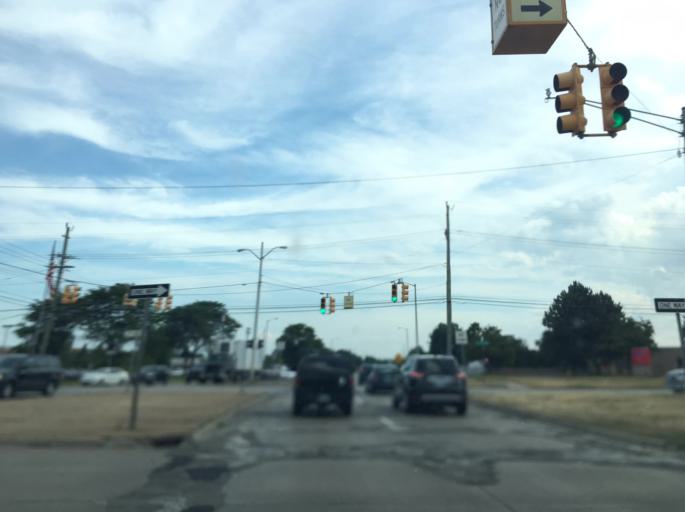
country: US
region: Michigan
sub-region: Macomb County
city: Sterling Heights
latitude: 42.5674
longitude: -82.9880
